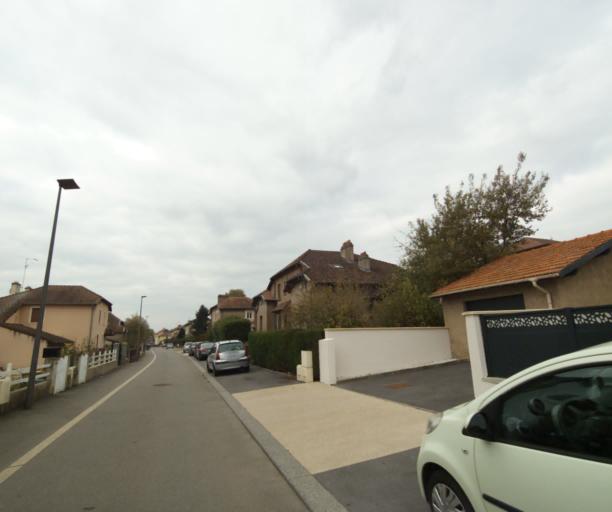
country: FR
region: Lorraine
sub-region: Departement de Meurthe-et-Moselle
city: Mancieulles
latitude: 49.2876
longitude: 5.9024
